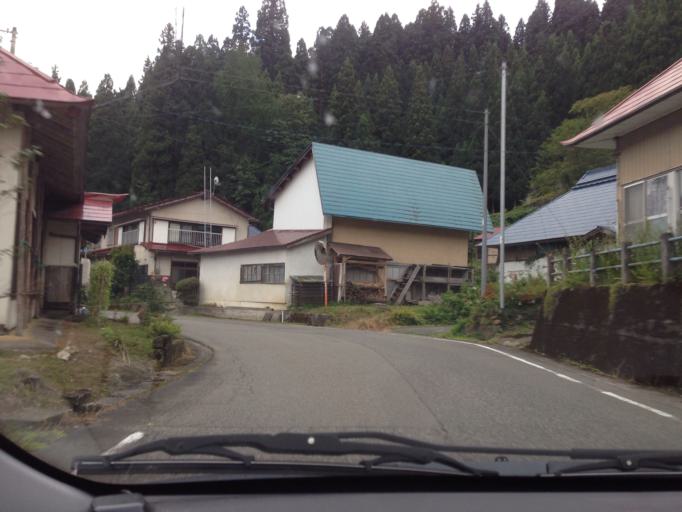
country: JP
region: Fukushima
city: Kitakata
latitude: 37.4554
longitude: 139.6469
